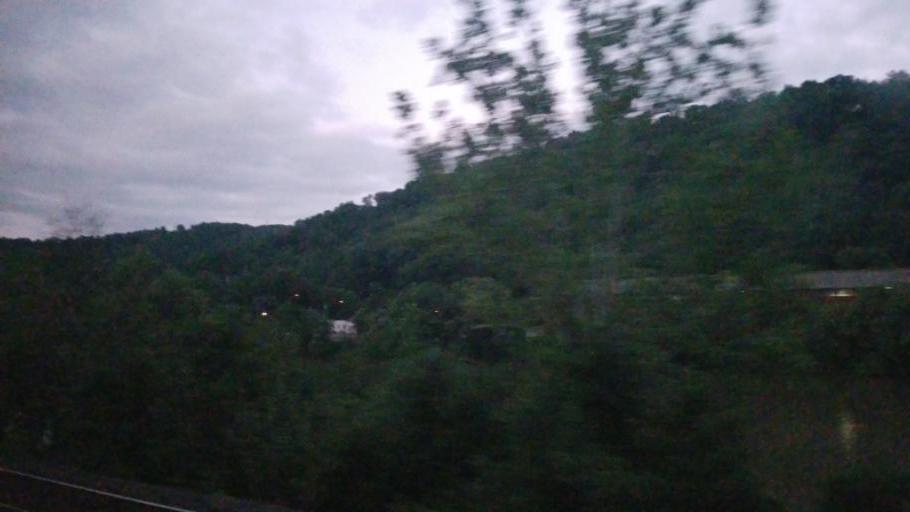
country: US
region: Pennsylvania
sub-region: Beaver County
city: New Brighton
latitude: 40.7261
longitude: -80.3082
